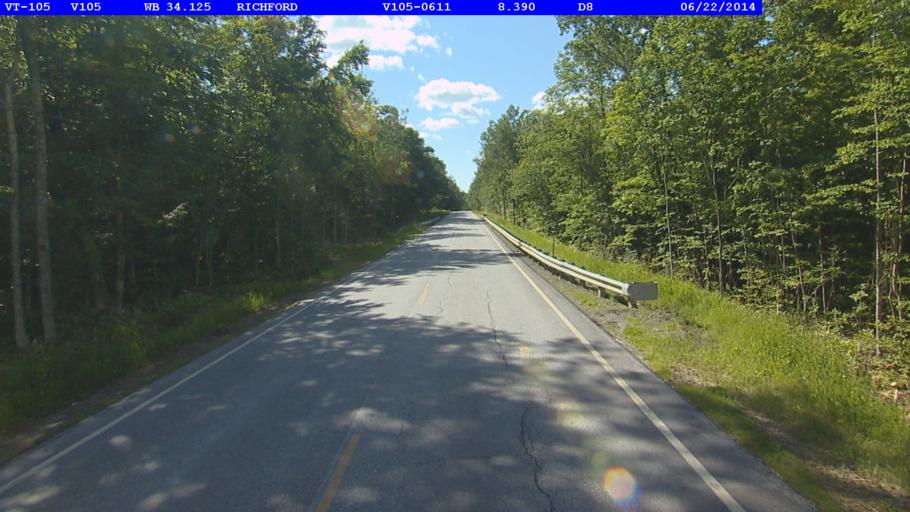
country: US
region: Vermont
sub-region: Franklin County
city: Richford
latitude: 44.9920
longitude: -72.5641
